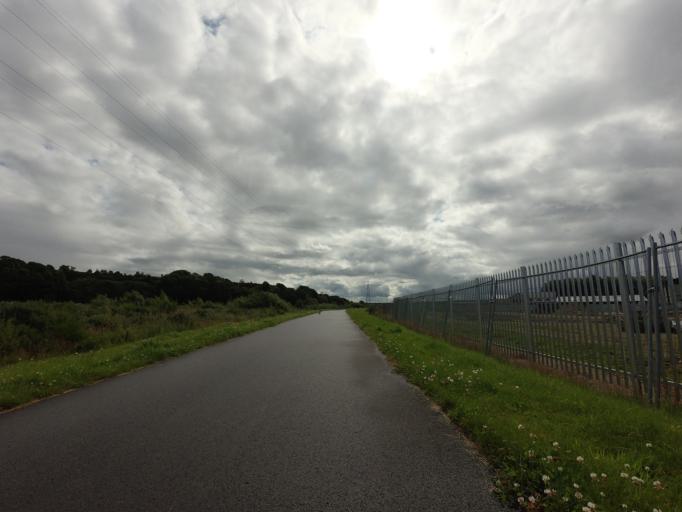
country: GB
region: Scotland
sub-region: Moray
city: Elgin
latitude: 57.6504
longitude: -3.2871
